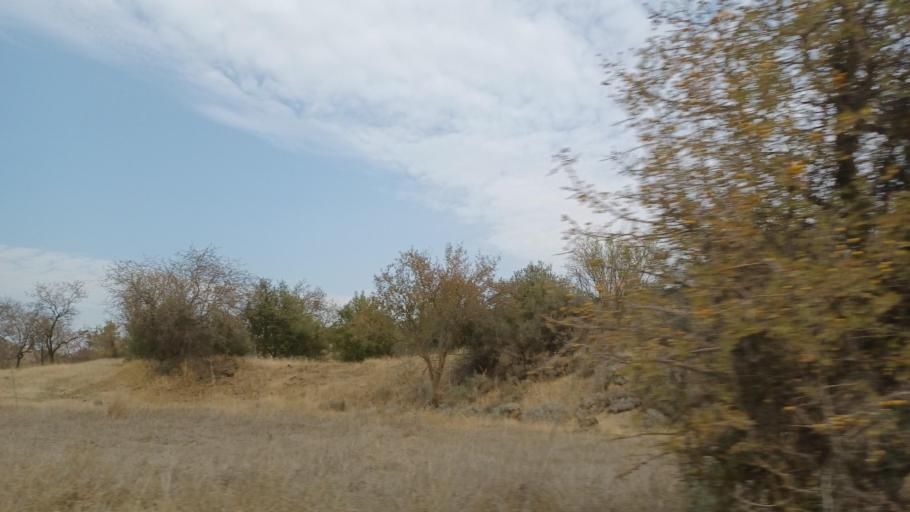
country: CY
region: Lefkosia
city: Klirou
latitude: 35.0327
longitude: 33.1362
